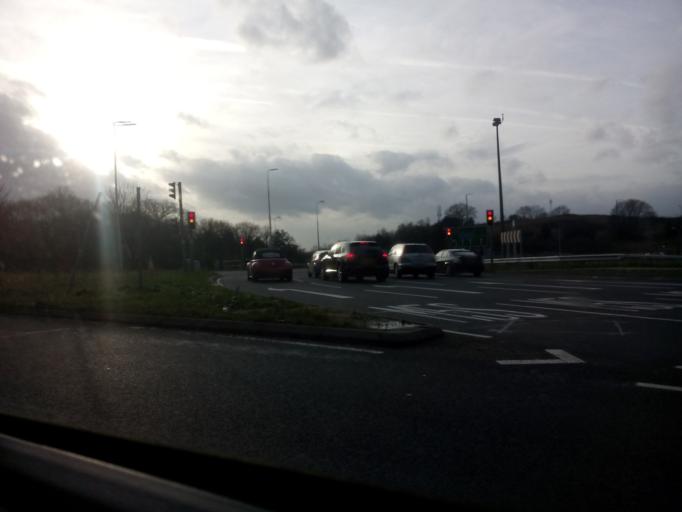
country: GB
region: England
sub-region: Worcestershire
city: Bromsgrove
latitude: 52.3774
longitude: -2.0468
